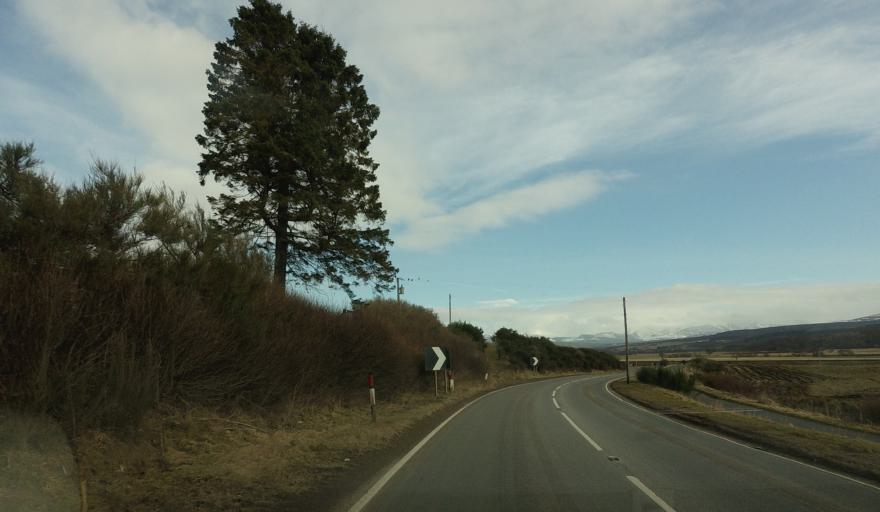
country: GB
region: Scotland
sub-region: Highland
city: Kingussie
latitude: 57.0728
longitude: -4.0958
